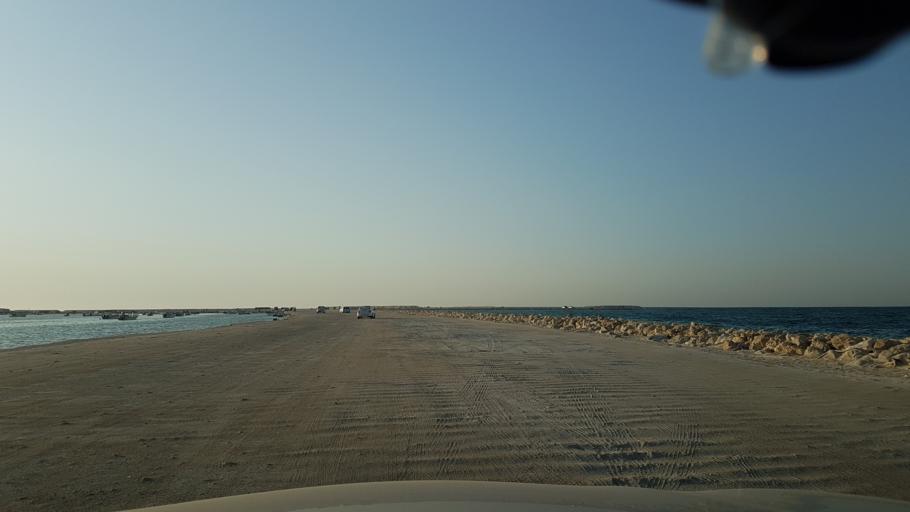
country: BH
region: Manama
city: Jidd Hafs
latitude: 26.2516
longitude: 50.5020
